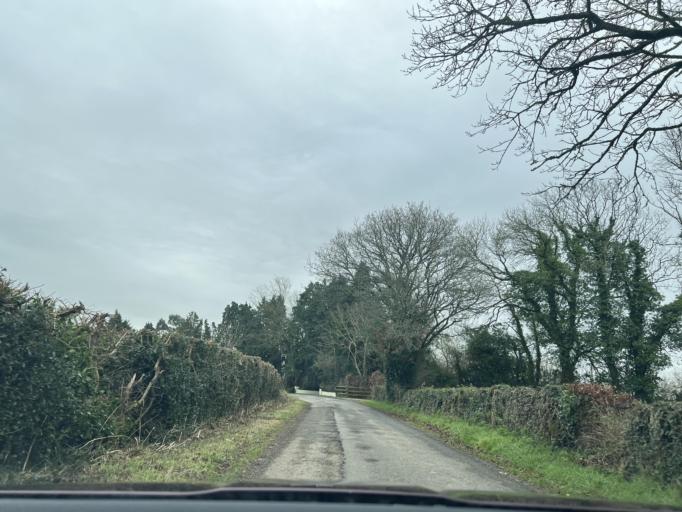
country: IE
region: Leinster
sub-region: Loch Garman
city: Castlebridge
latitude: 52.3869
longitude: -6.5302
